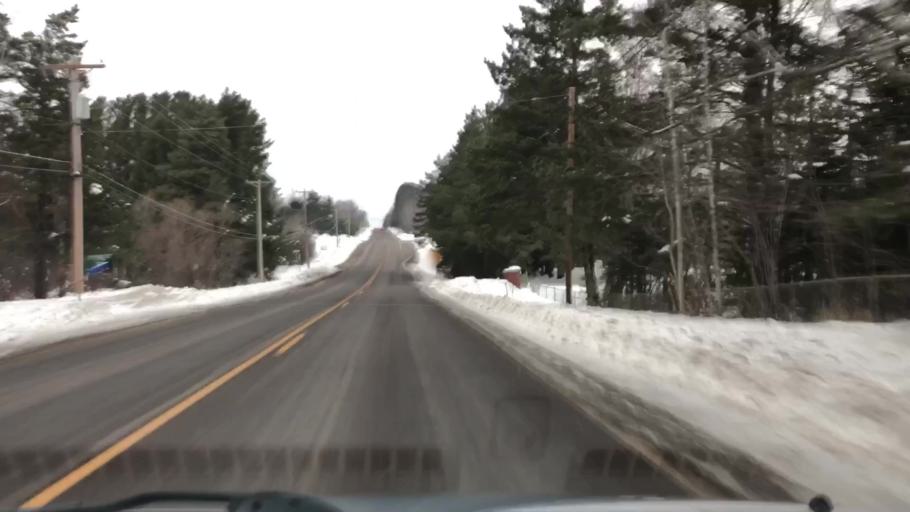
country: US
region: Minnesota
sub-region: Saint Louis County
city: Arnold
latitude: 46.8631
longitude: -92.1111
